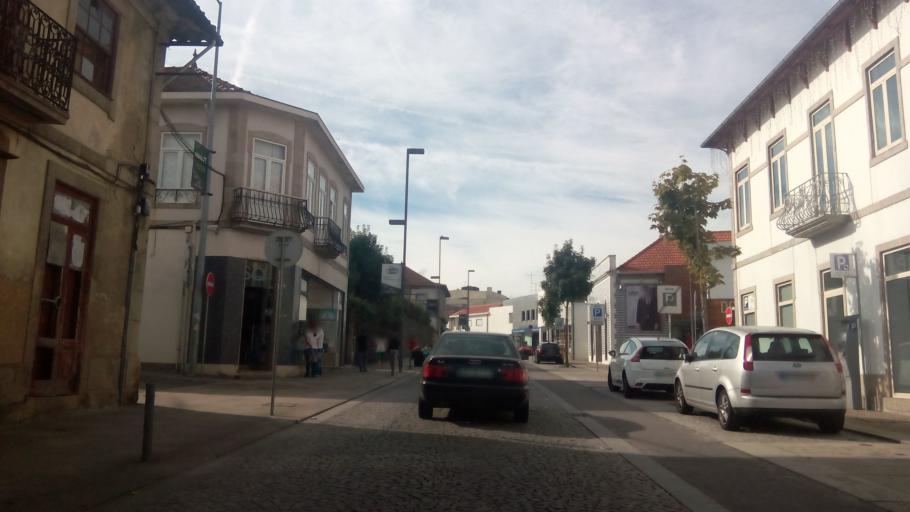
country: PT
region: Porto
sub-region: Paredes
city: Paredes
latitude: 41.2070
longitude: -8.3305
